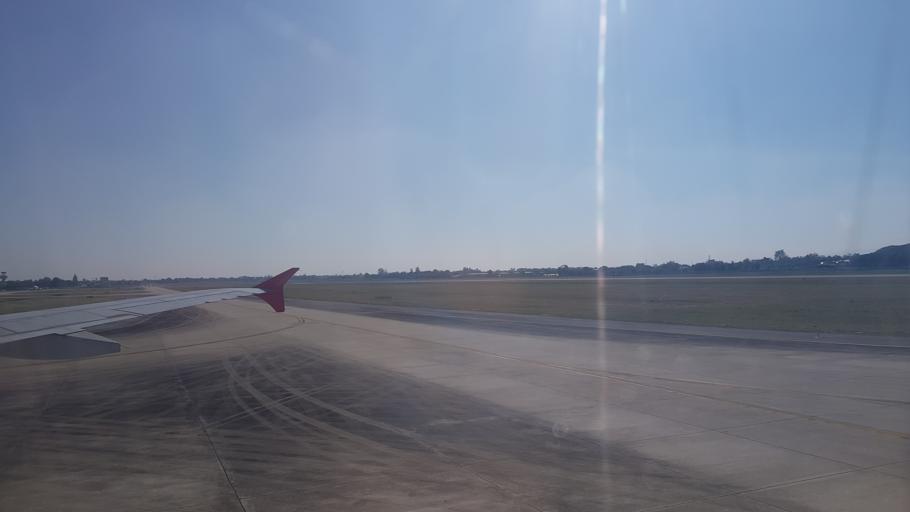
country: TH
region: Chiang Mai
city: Chiang Mai
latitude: 18.7711
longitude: 98.9656
